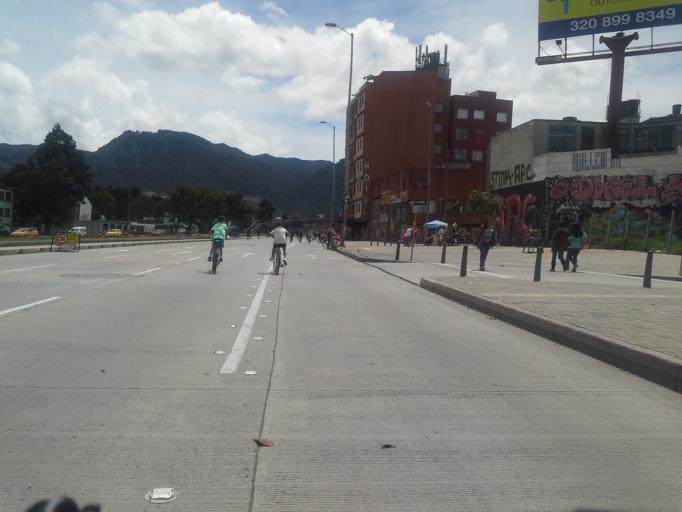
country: CO
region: Bogota D.C.
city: Bogota
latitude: 4.6330
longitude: -74.0867
